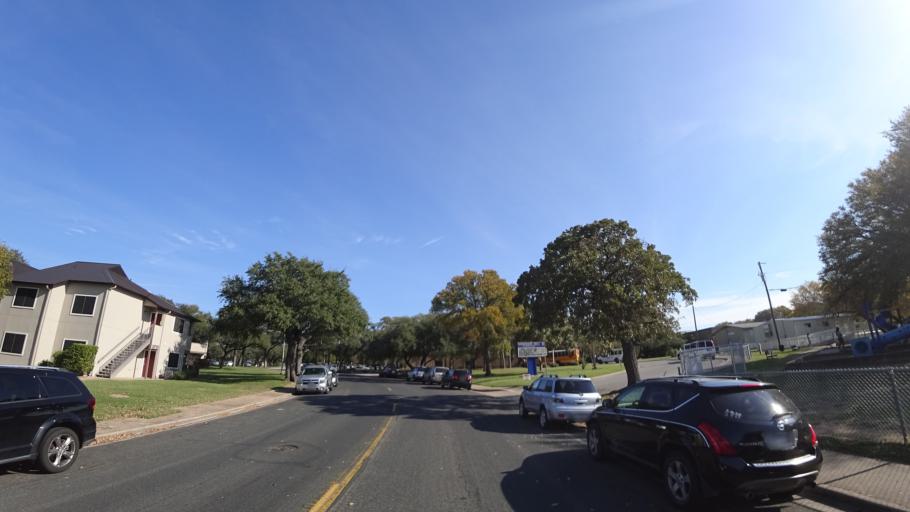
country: US
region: Texas
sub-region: Williamson County
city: Anderson Mill
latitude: 30.4536
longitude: -97.8071
